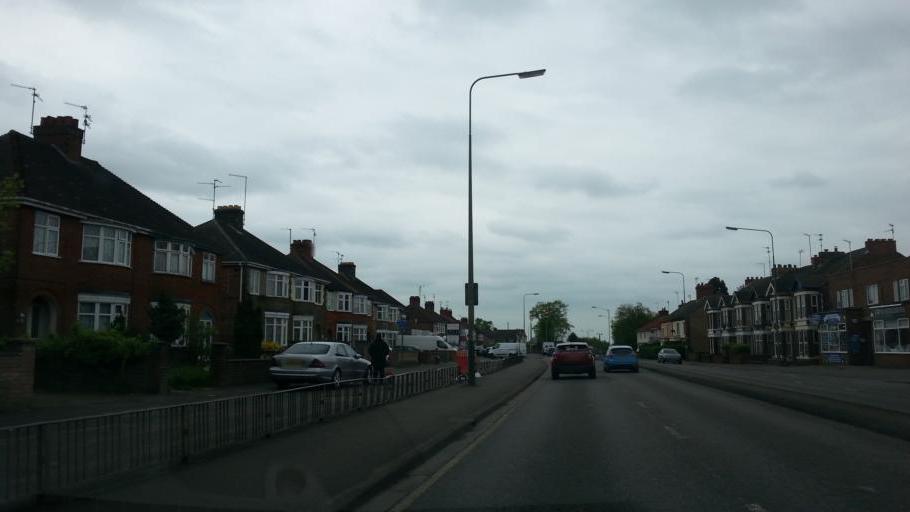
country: GB
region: England
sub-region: Peterborough
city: Peterborough
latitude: 52.6021
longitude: -0.2671
